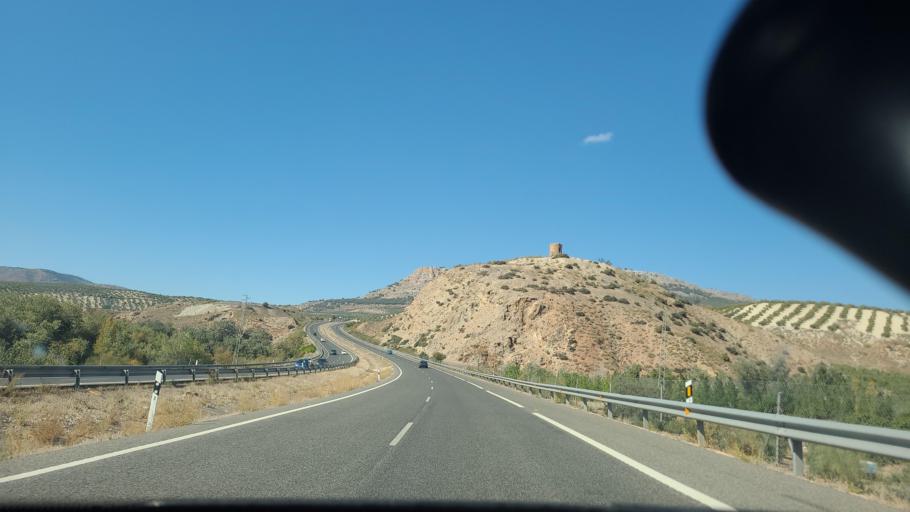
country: ES
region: Andalusia
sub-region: Provincia de Jaen
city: Pegalajar
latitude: 37.7096
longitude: -3.6397
